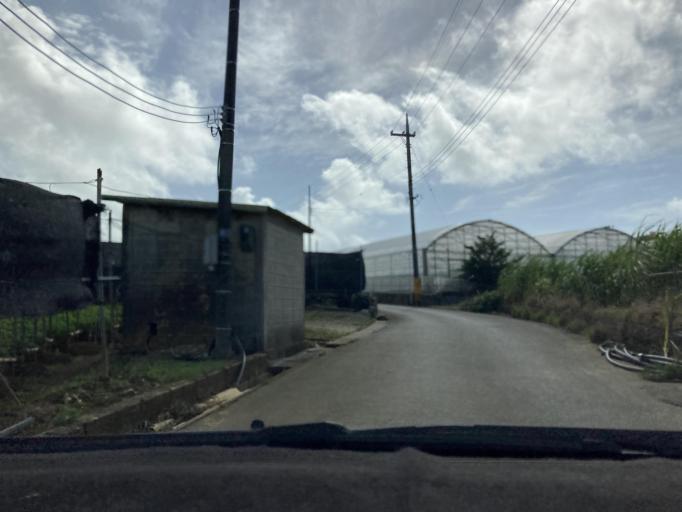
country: JP
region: Okinawa
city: Itoman
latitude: 26.0979
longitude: 127.6630
